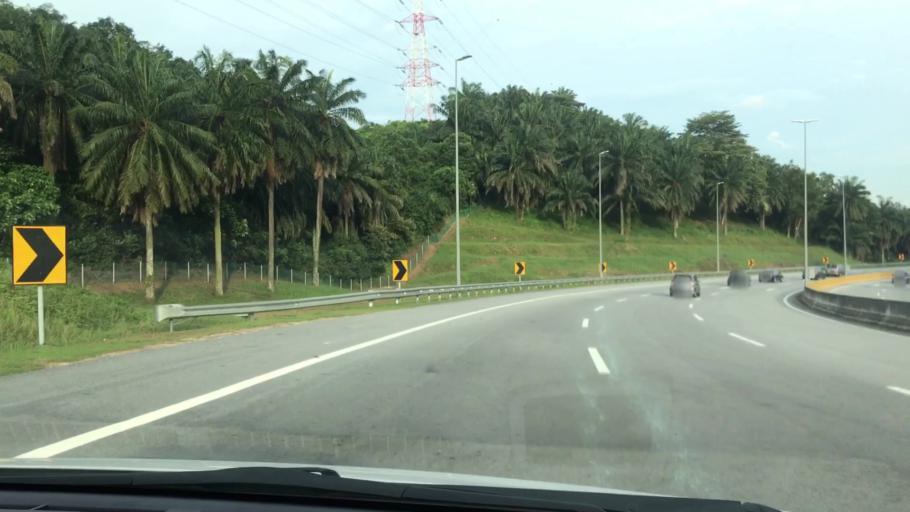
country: MY
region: Selangor
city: Kampong Baharu Balakong
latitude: 3.0124
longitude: 101.6853
